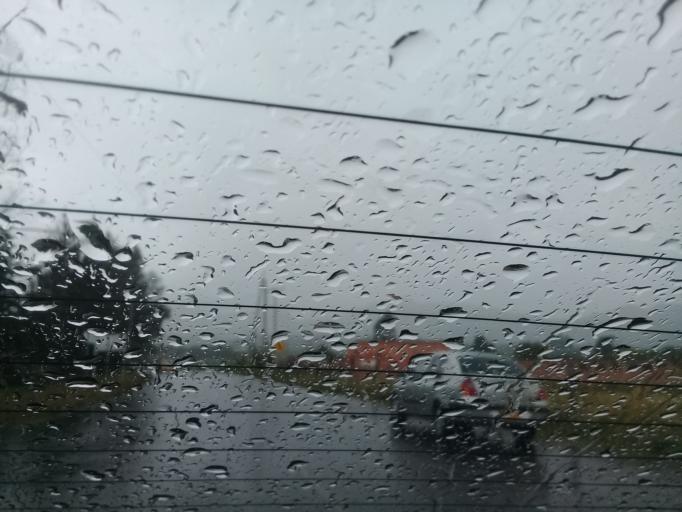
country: CO
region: Cundinamarca
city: Guasca
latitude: 4.8653
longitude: -73.8701
